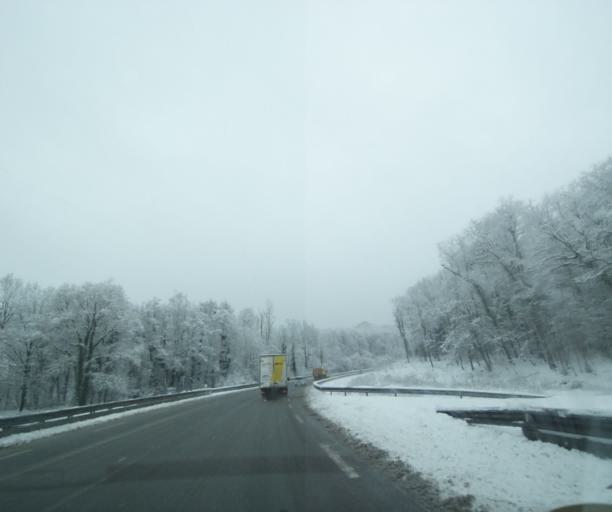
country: FR
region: Champagne-Ardenne
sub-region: Departement de la Haute-Marne
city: Saint-Dizier
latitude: 48.6150
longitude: 4.9179
